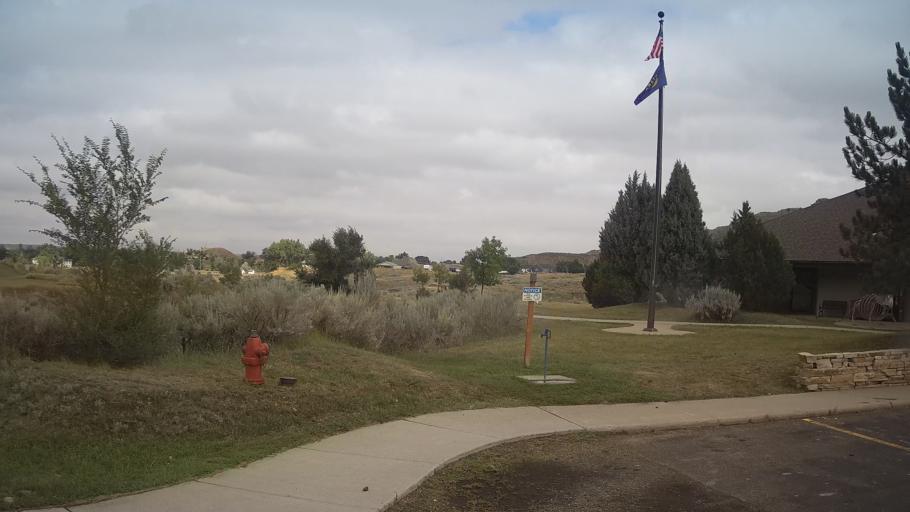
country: US
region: Montana
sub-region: Dawson County
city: Glendive
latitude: 47.0893
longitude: -104.7067
